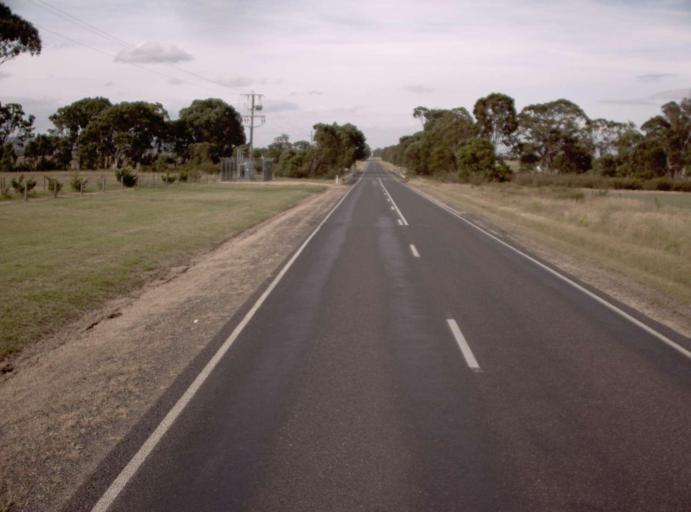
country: AU
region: Victoria
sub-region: Wellington
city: Heyfield
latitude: -38.0502
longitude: 146.6639
